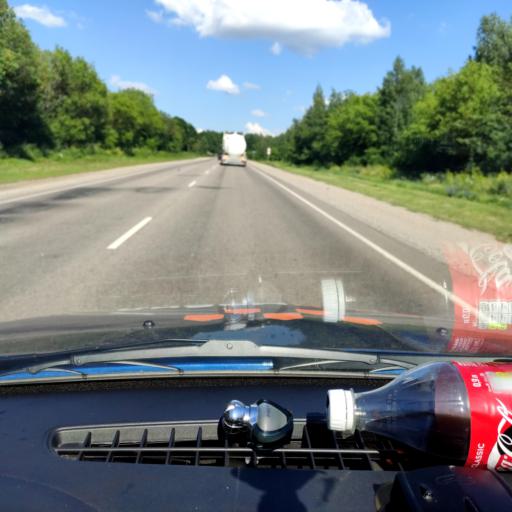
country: RU
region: Lipetsk
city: Kazaki
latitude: 52.6370
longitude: 38.2961
